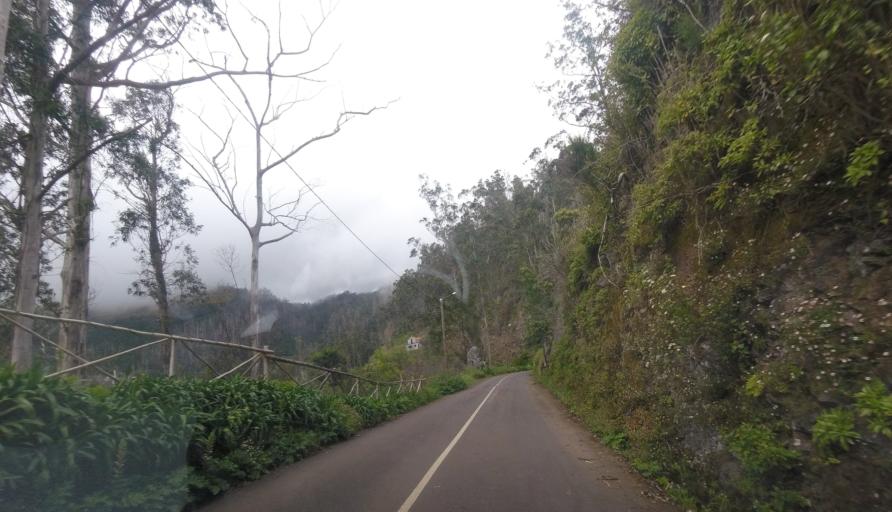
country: PT
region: Madeira
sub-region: Funchal
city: Nossa Senhora do Monte
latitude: 32.6846
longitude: -16.8913
